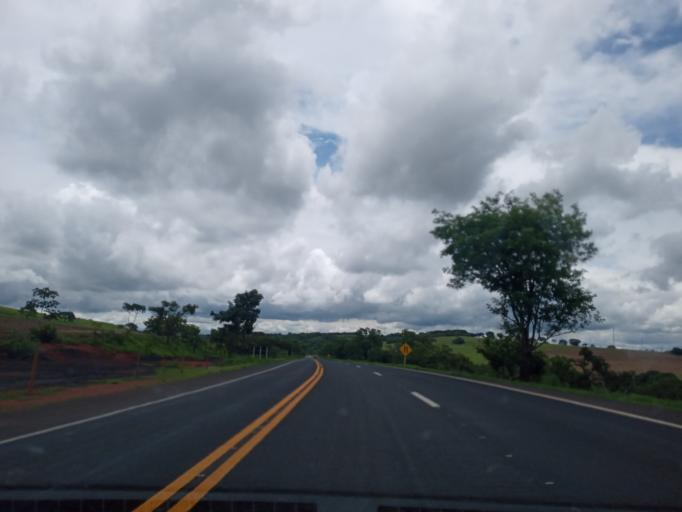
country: BR
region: Minas Gerais
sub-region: Monte Carmelo
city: Monte Carmelo
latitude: -19.2610
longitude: -47.6521
